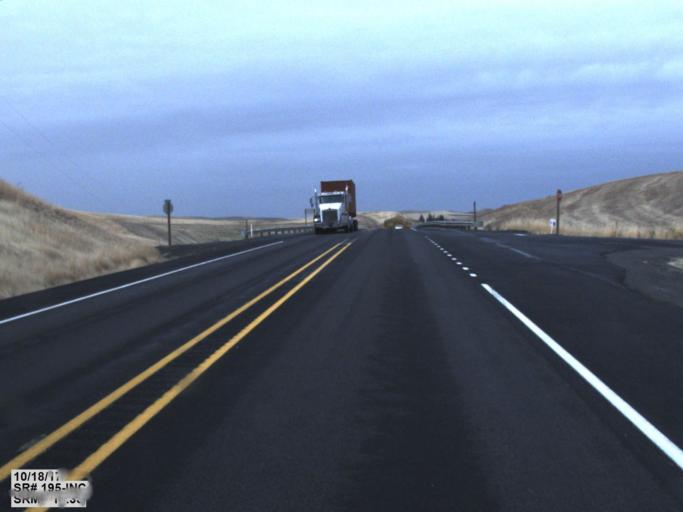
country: US
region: Washington
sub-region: Whitman County
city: Pullman
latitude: 46.6219
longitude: -117.1659
